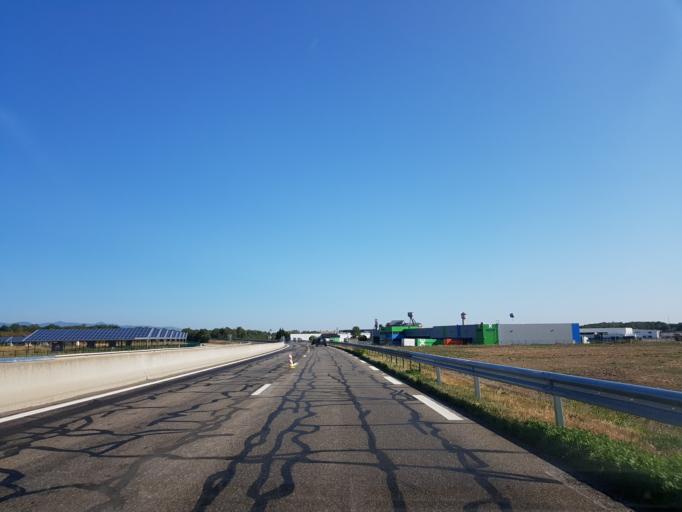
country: FR
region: Alsace
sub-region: Departement du Haut-Rhin
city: Pulversheim
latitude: 47.8375
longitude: 7.2764
